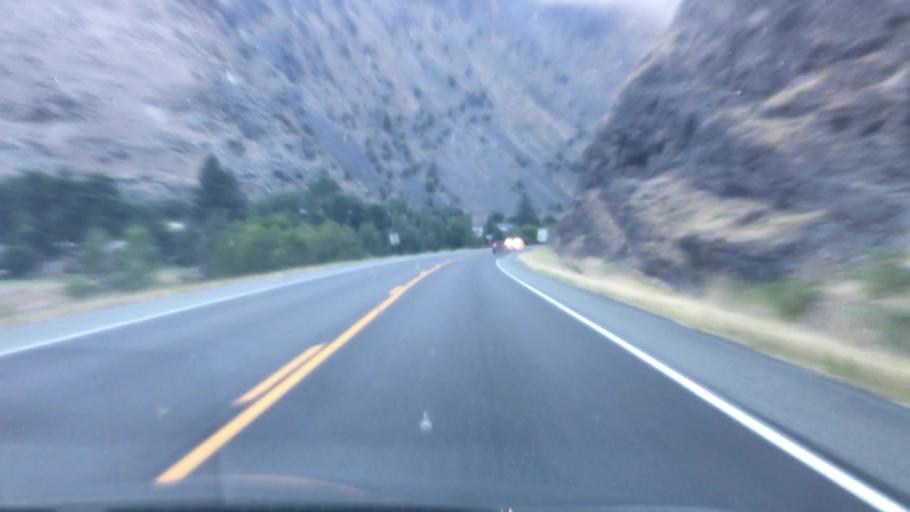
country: US
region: Idaho
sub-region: Valley County
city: McCall
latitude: 45.3551
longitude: -116.3592
